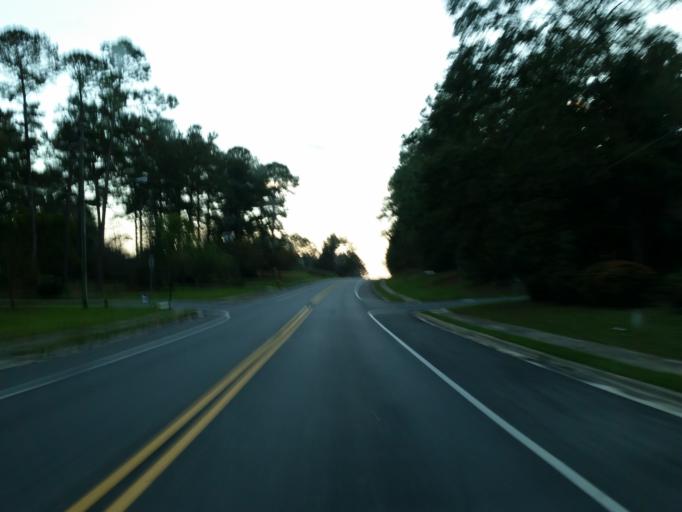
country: US
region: Georgia
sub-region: Pulaski County
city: Hawkinsville
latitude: 32.2725
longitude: -83.4794
